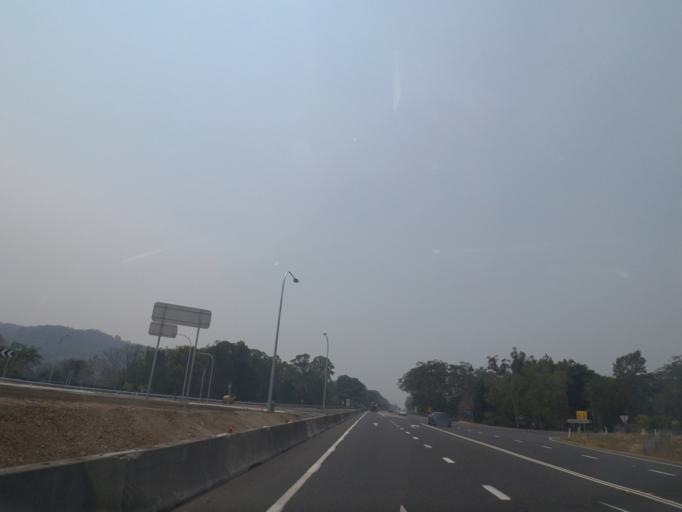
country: AU
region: New South Wales
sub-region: Ballina
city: Ballina
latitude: -28.9226
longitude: 153.4760
